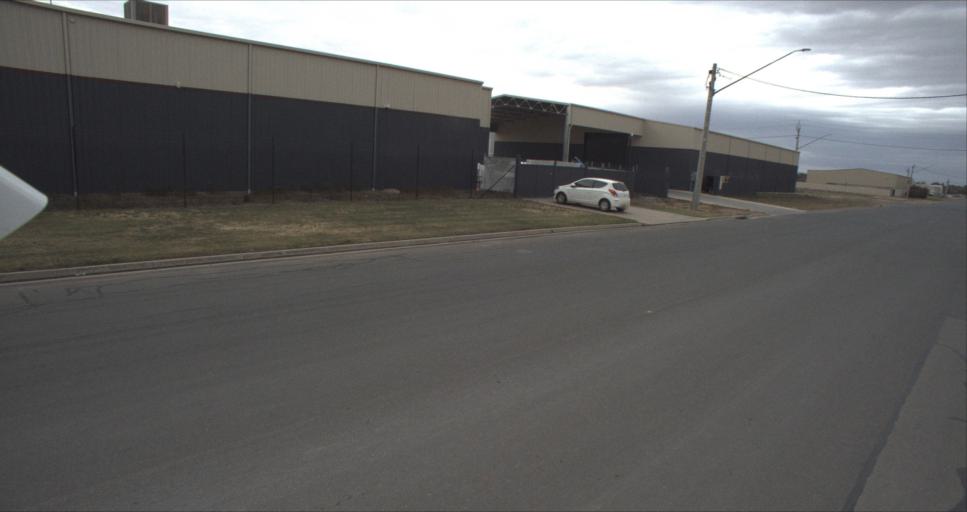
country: AU
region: New South Wales
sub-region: Leeton
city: Leeton
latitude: -34.5457
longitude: 146.3867
